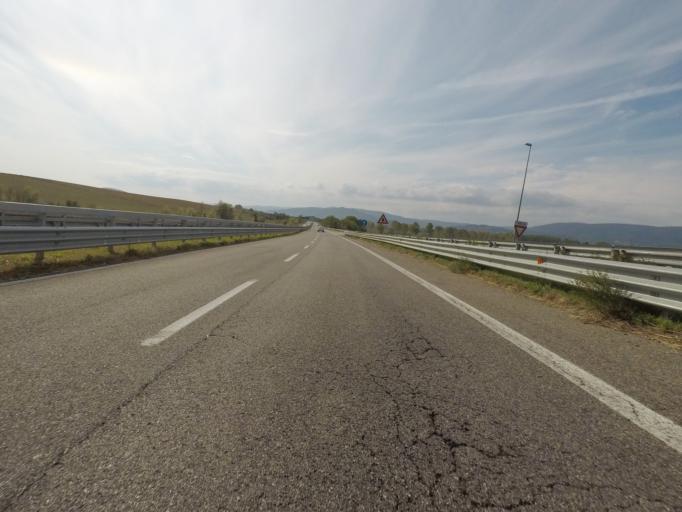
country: IT
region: Tuscany
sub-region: Provincia di Siena
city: Rosia
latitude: 43.2400
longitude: 11.2806
